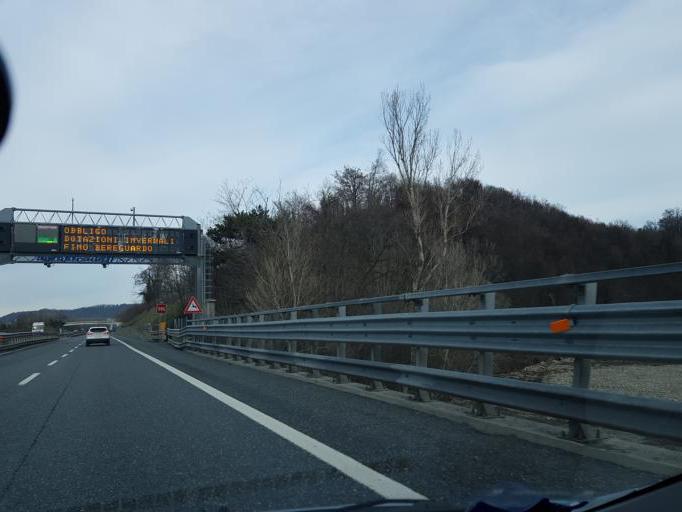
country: IT
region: Piedmont
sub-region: Provincia di Alessandria
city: Arquata Scrivia
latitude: 44.6928
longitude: 8.8984
